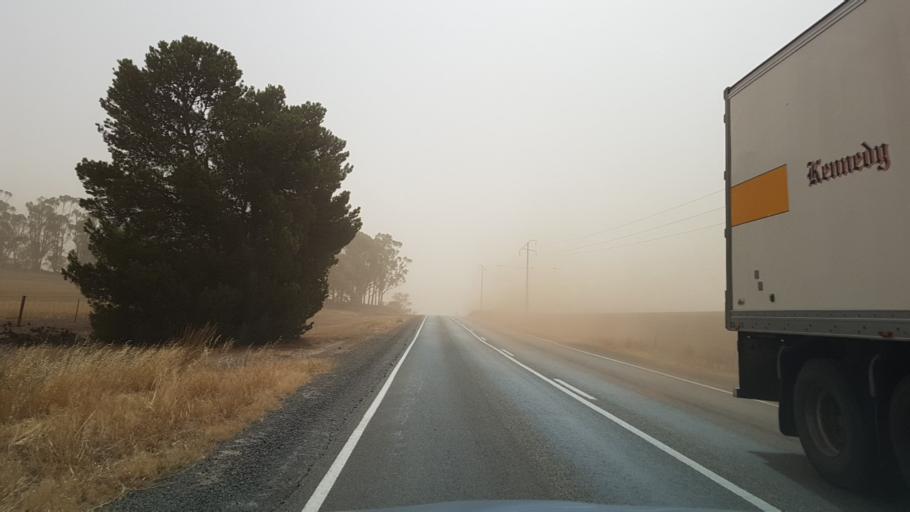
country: AU
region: South Australia
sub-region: Clare and Gilbert Valleys
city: Clare
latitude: -33.8374
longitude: 138.8627
